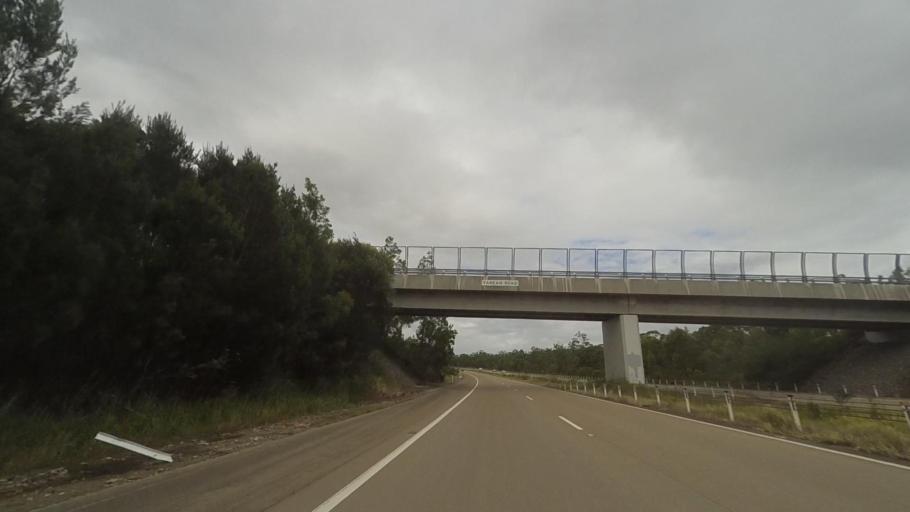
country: AU
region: New South Wales
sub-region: Port Stephens Shire
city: Medowie
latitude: -32.6466
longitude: 151.9211
